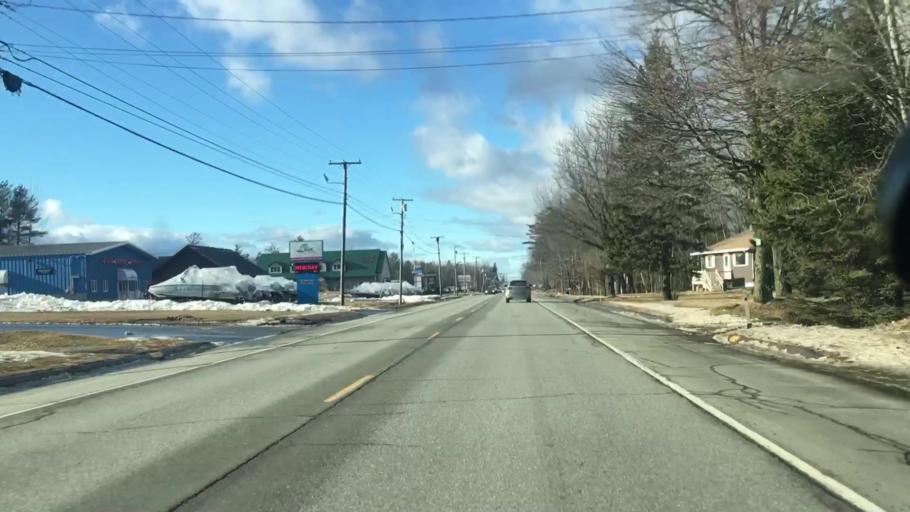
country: US
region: Maine
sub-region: Penobscot County
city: Holden
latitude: 44.7593
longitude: -68.6931
